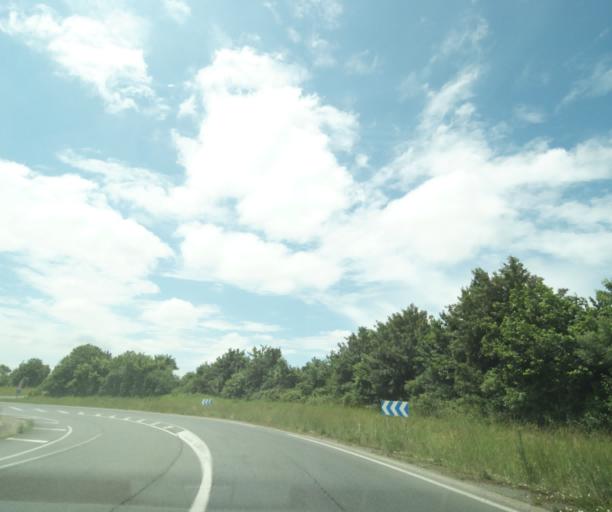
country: FR
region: Poitou-Charentes
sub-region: Departement des Deux-Sevres
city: Echire
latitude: 46.4245
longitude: -0.3983
